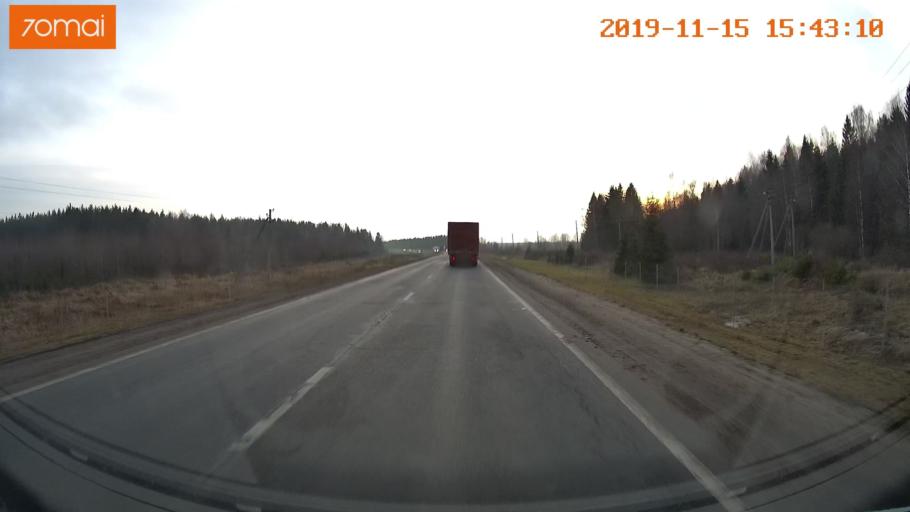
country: RU
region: Jaroslavl
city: Danilov
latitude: 57.9854
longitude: 40.0309
